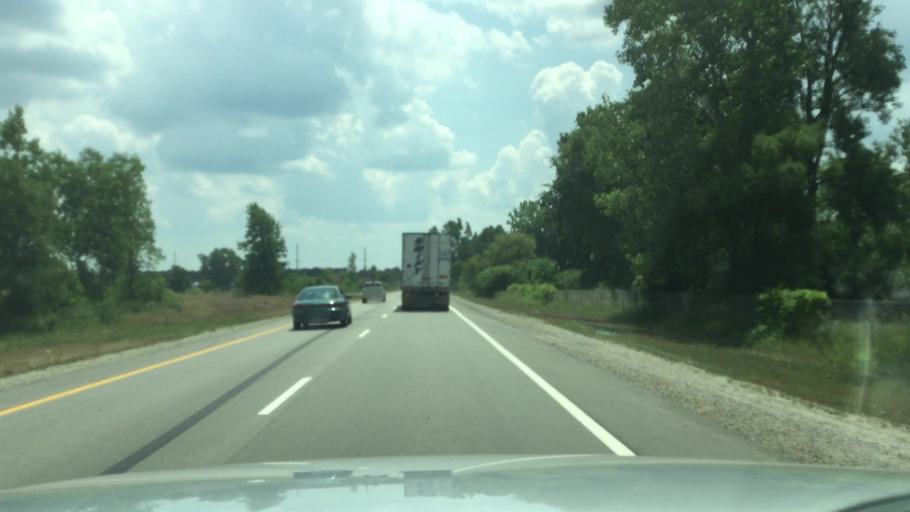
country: US
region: Michigan
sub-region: Washtenaw County
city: Ypsilanti
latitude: 42.2353
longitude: -83.5631
